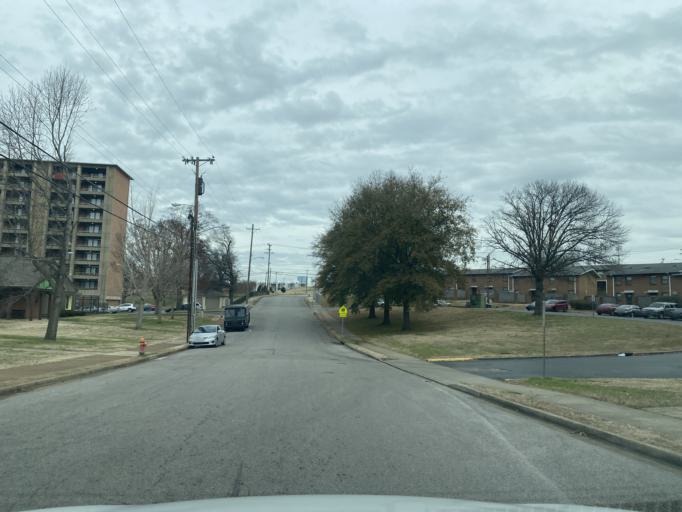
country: US
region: Tennessee
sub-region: Davidson County
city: Nashville
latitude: 36.1409
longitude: -86.7857
